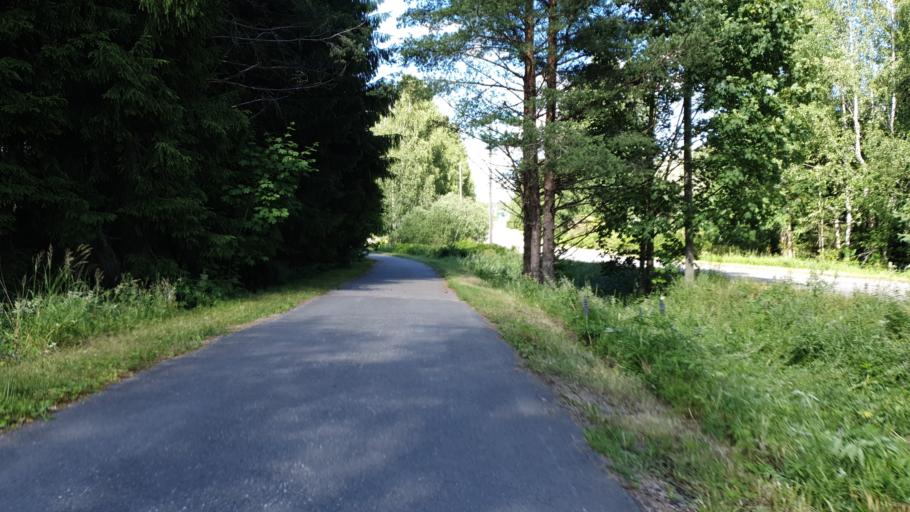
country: FI
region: Uusimaa
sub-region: Helsinki
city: Tuusula
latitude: 60.3658
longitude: 25.0097
